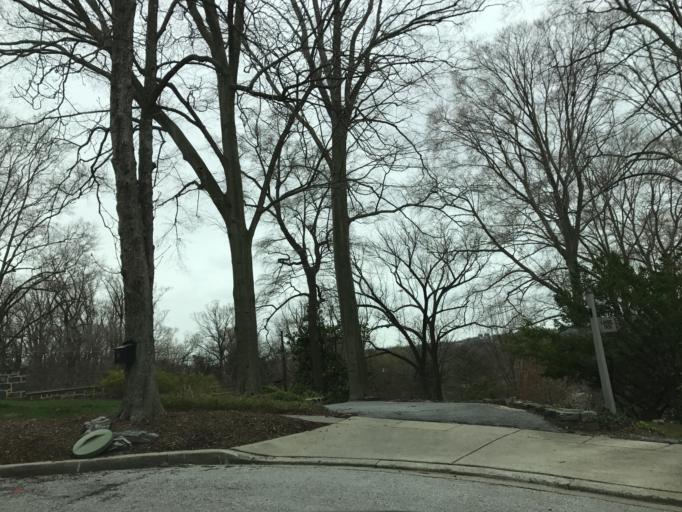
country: US
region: Maryland
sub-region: Baltimore County
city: Towson
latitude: 39.3568
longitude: -76.6411
